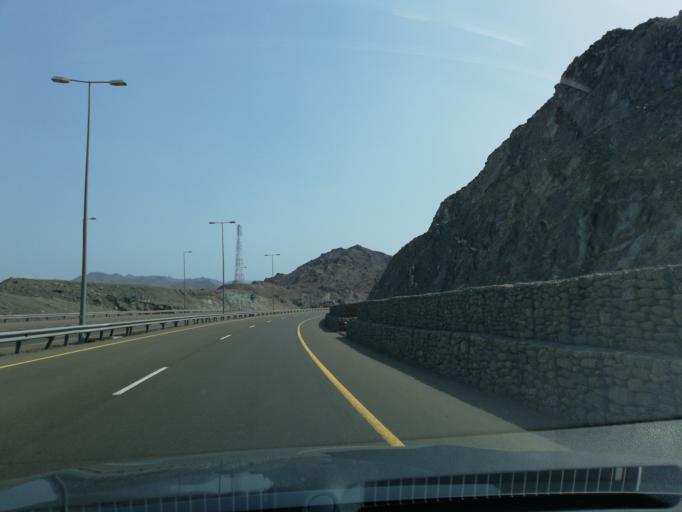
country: OM
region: Al Batinah
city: Al Liwa'
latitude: 24.2395
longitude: 56.3480
